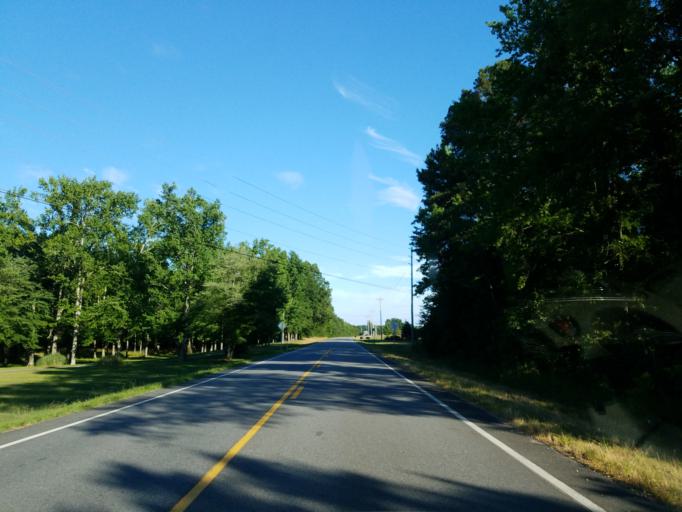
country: US
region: Georgia
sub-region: Gordon County
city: Calhoun
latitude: 34.5952
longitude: -85.0407
